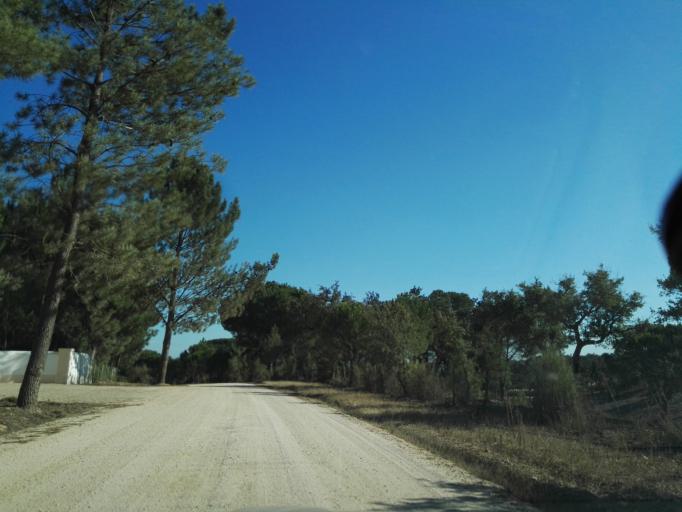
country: PT
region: Santarem
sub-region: Benavente
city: Poceirao
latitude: 38.8748
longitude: -8.7388
